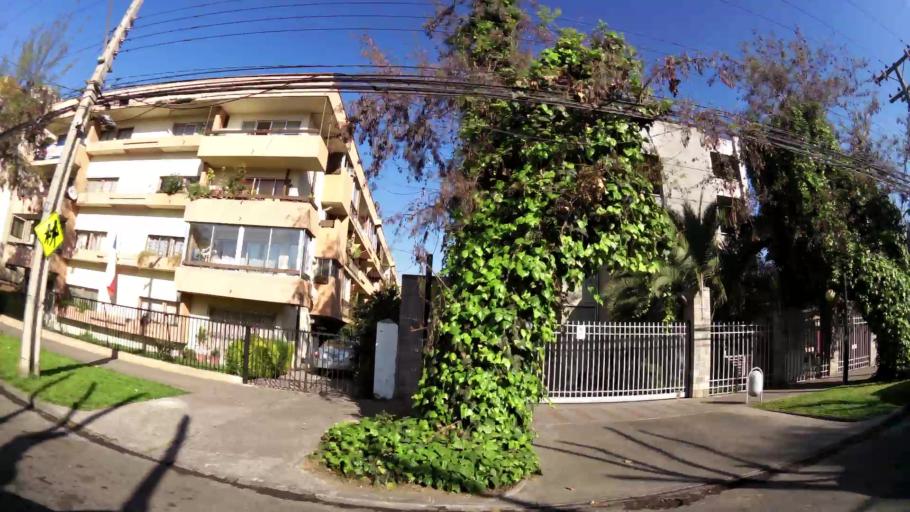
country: CL
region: Santiago Metropolitan
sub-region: Provincia de Santiago
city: Villa Presidente Frei, Nunoa, Santiago, Chile
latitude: -33.4530
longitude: -70.5918
